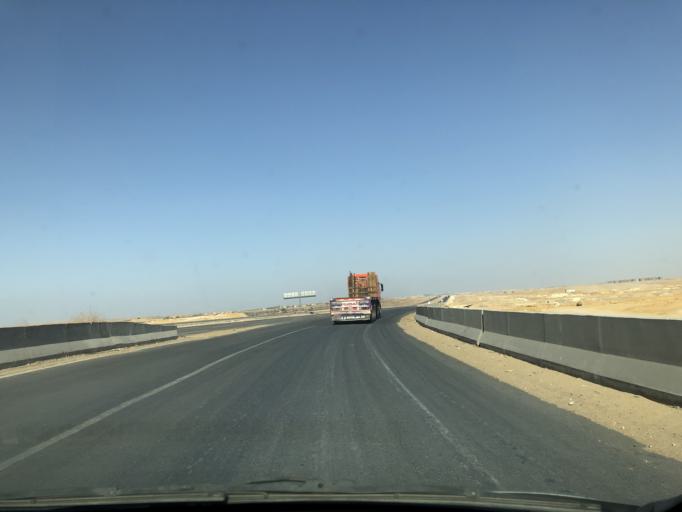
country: EG
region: Muhafazat al Minufiyah
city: Ashmun
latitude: 30.0672
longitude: 30.8476
